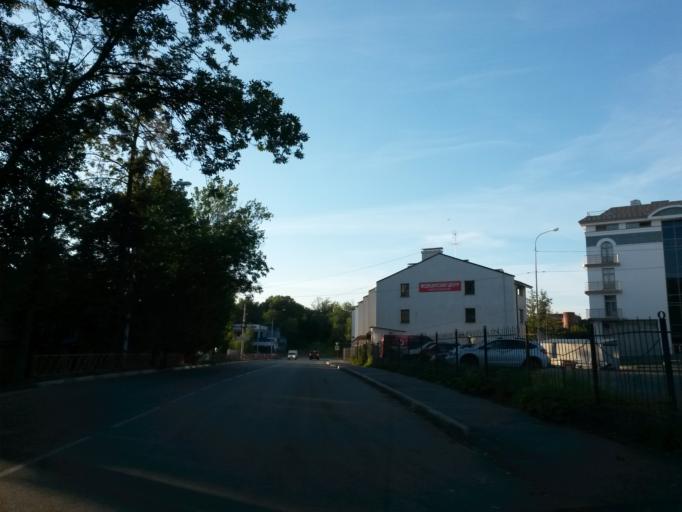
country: RU
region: Jaroslavl
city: Yaroslavl
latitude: 57.6111
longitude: 39.8807
